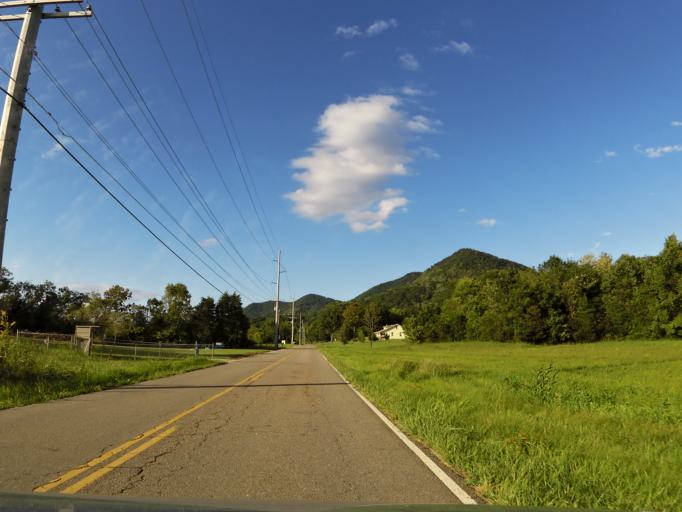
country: US
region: Tennessee
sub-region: Grainger County
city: Blaine
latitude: 36.1565
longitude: -83.7376
